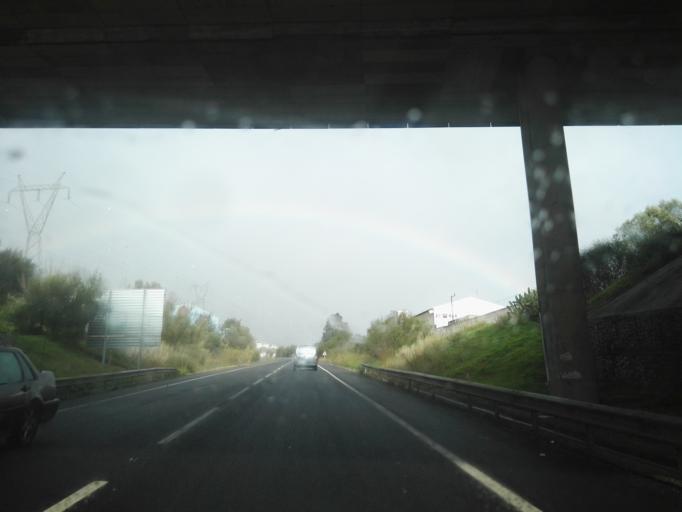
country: PT
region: Lisbon
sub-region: Vila Franca de Xira
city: Vialonga
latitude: 38.8955
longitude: -9.0514
